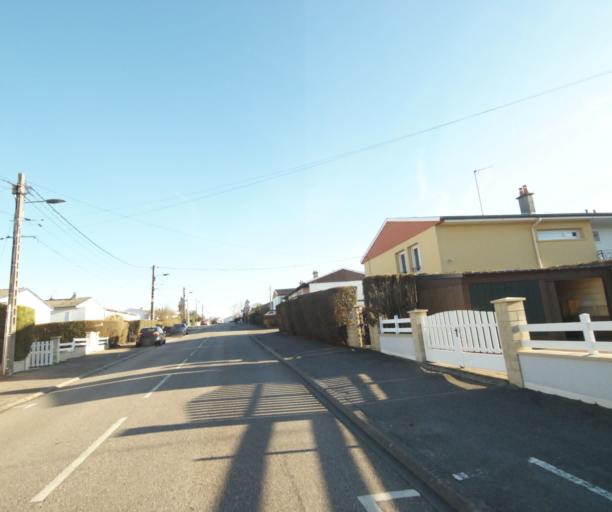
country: FR
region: Lorraine
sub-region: Departement de Meurthe-et-Moselle
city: Seichamps
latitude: 48.7147
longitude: 6.2647
